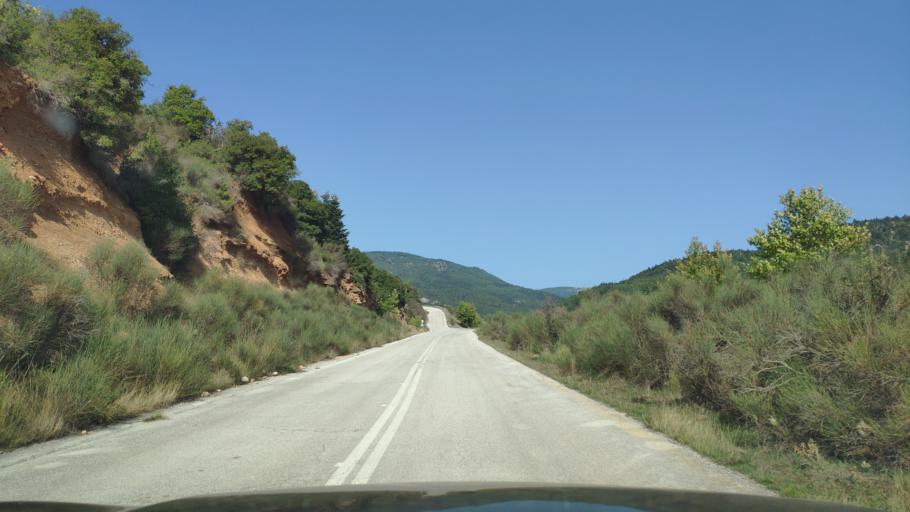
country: GR
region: West Greece
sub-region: Nomos Achaias
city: Aiyira
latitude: 37.9835
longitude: 22.3567
